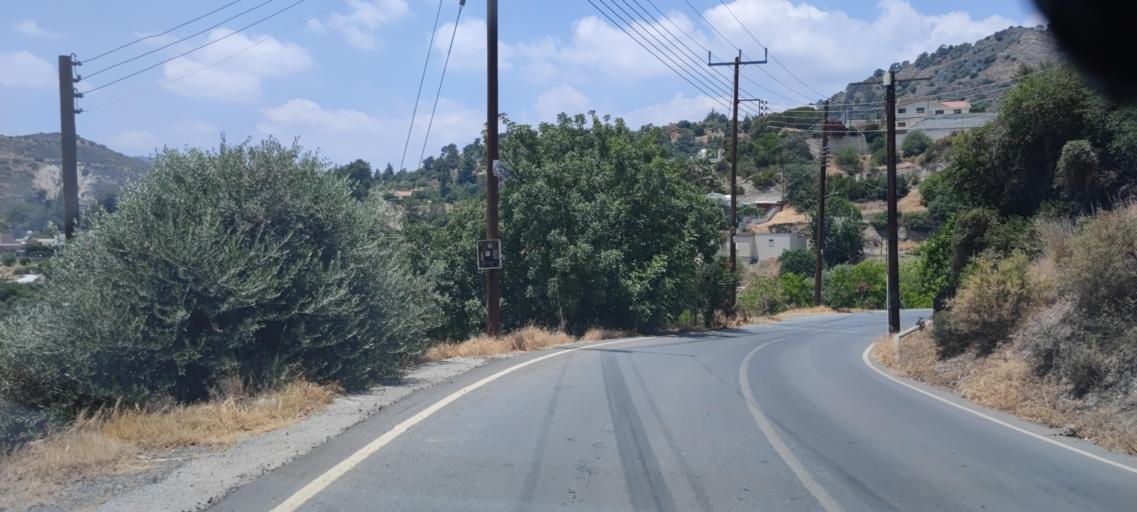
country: CY
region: Limassol
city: Pano Polemidia
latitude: 34.7980
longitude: 33.0218
